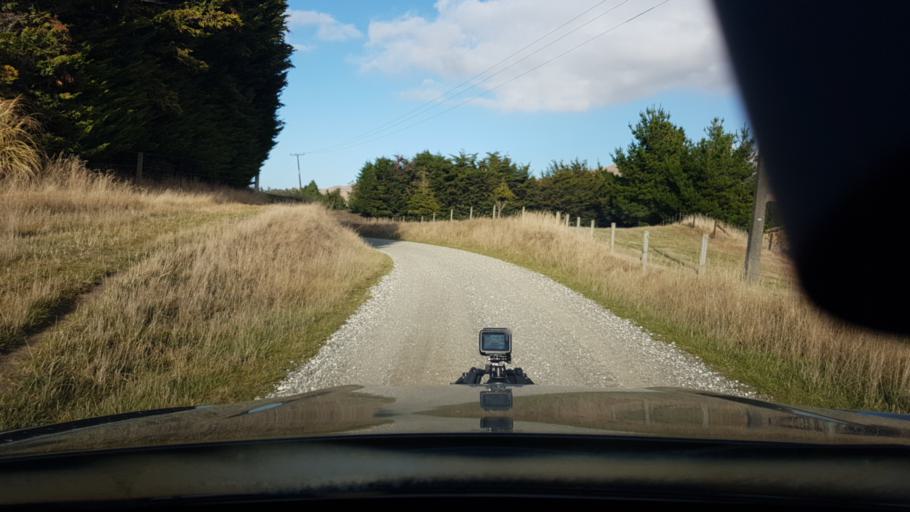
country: NZ
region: Marlborough
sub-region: Marlborough District
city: Blenheim
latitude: -41.8405
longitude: 174.1237
